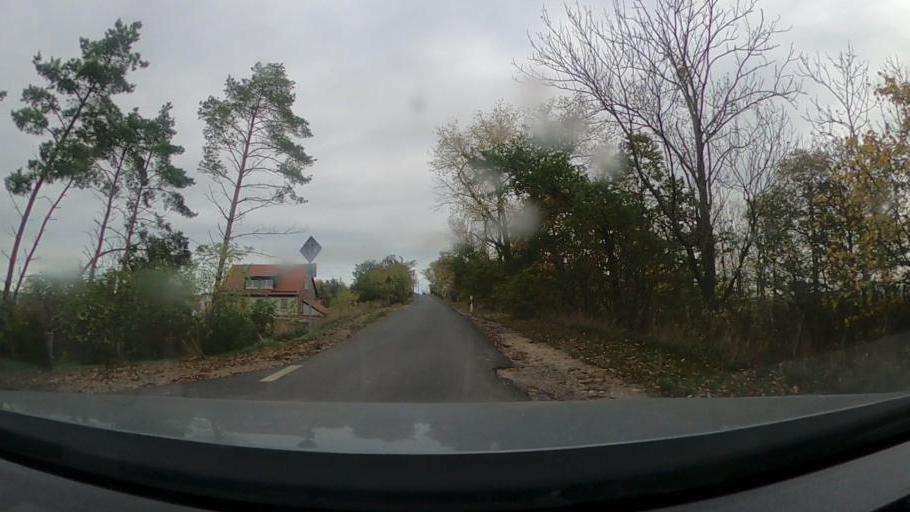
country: DE
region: Thuringia
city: Bad Sulza
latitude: 51.1060
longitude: 11.6393
